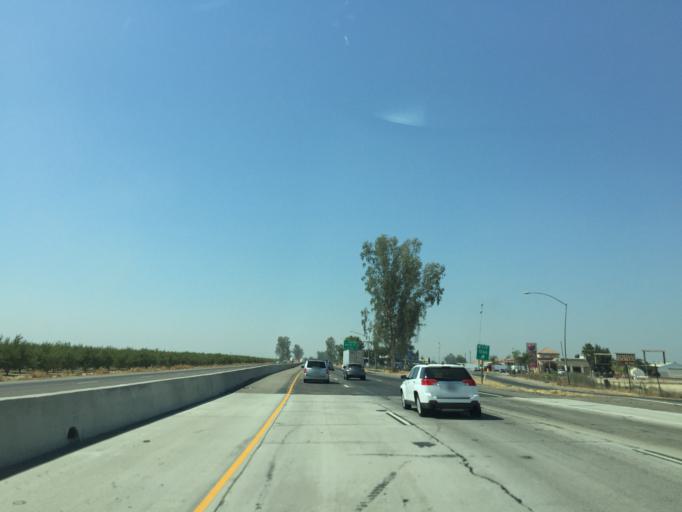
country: US
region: California
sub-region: Tulare County
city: London
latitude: 36.4456
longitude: -119.4841
